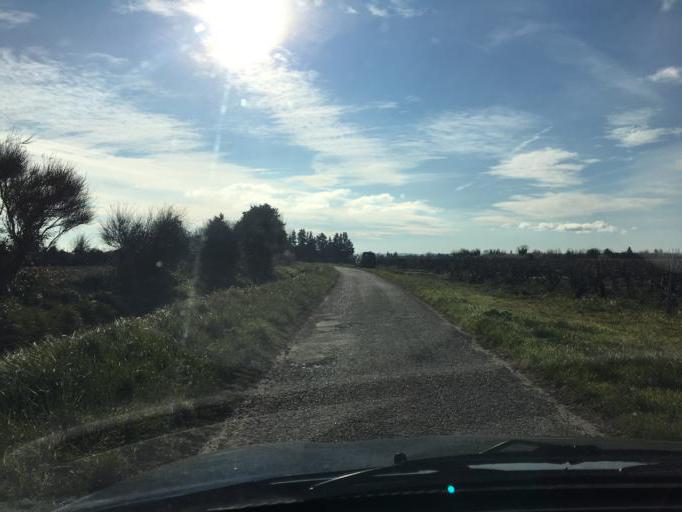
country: FR
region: Provence-Alpes-Cote d'Azur
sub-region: Departement du Vaucluse
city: Camaret-sur-Aigues
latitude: 44.1593
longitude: 4.8903
